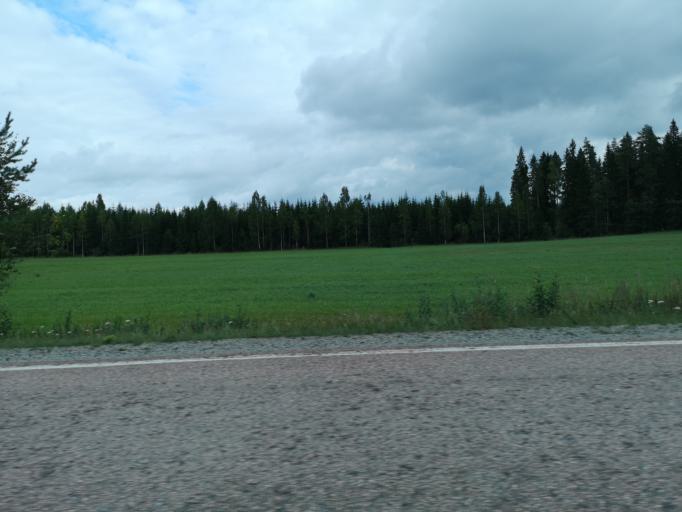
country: FI
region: Central Finland
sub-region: Jyvaeskylae
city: Hankasalmi
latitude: 62.3613
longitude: 26.5431
